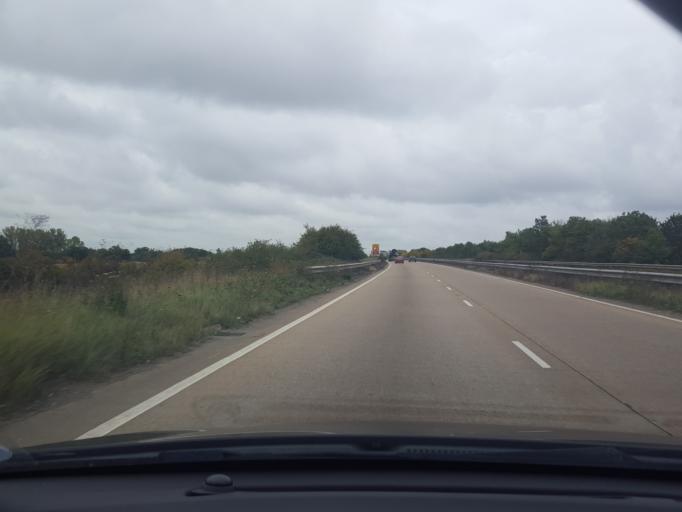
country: GB
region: England
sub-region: Essex
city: Great Bentley
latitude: 51.8785
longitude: 1.0492
